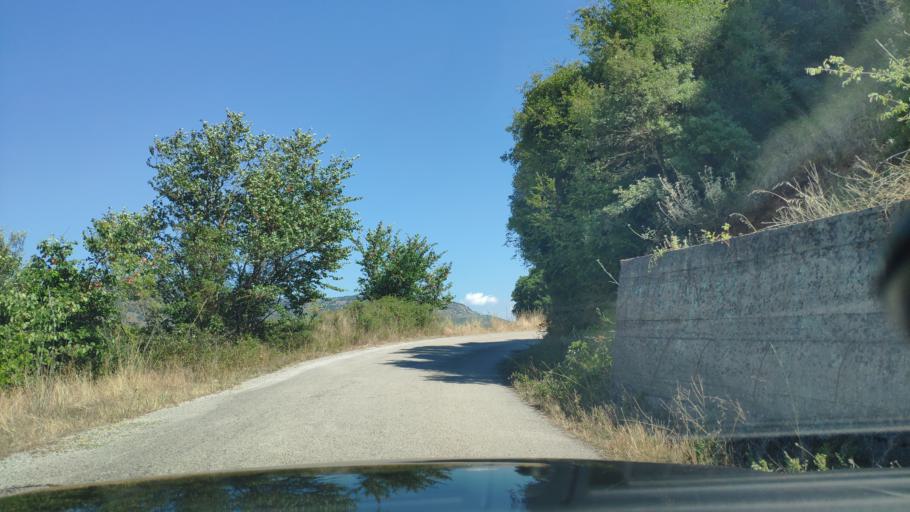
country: GR
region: West Greece
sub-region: Nomos Aitolias kai Akarnanias
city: Katouna
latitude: 38.8225
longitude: 21.1026
